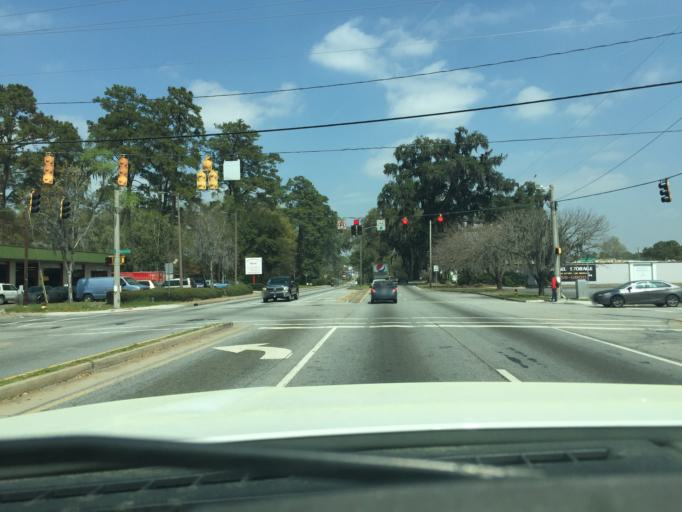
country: US
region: Georgia
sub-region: Chatham County
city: Savannah
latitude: 32.0253
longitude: -81.1121
